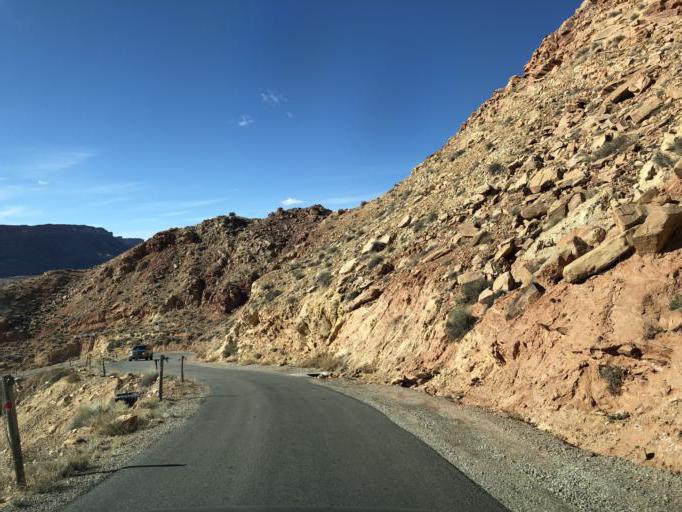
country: US
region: Utah
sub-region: Grand County
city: Moab
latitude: 38.5887
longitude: -109.5556
